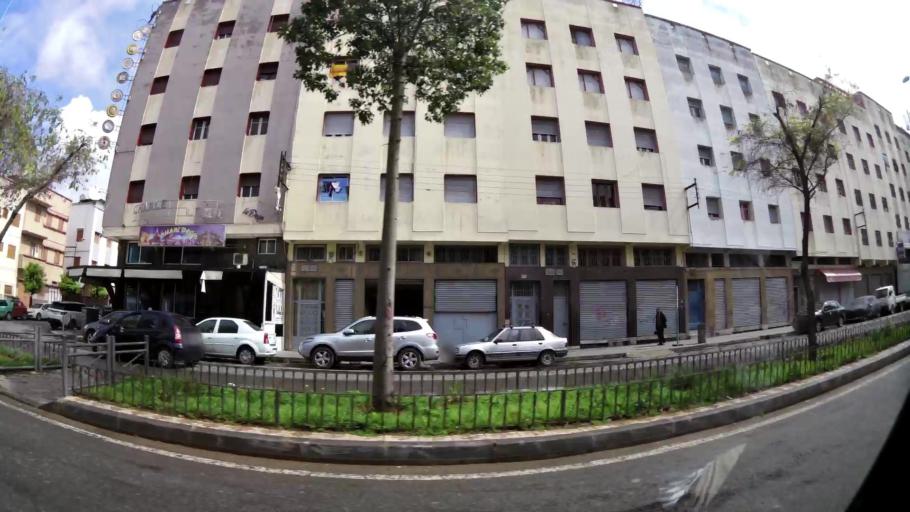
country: MA
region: Grand Casablanca
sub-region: Casablanca
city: Casablanca
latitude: 33.5437
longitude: -7.5684
